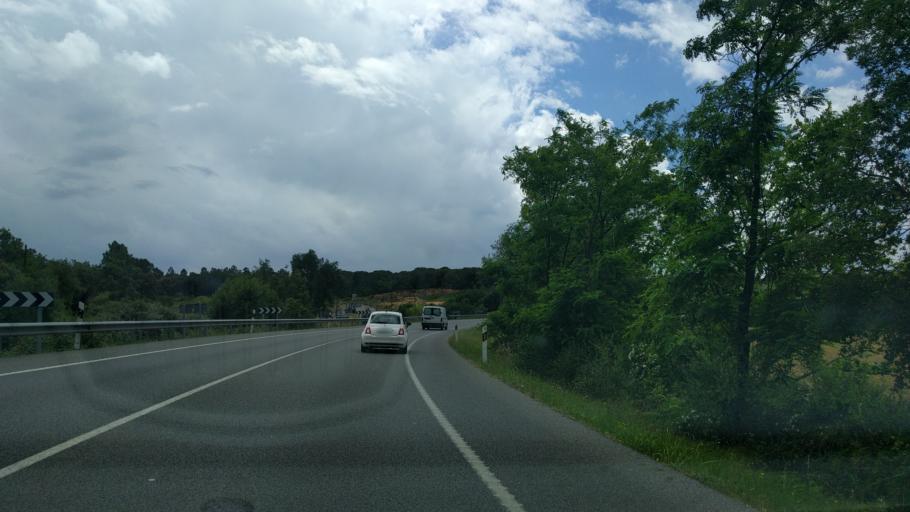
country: ES
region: Catalonia
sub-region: Provincia de Girona
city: Macanet de la Selva
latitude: 41.7509
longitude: 2.7560
